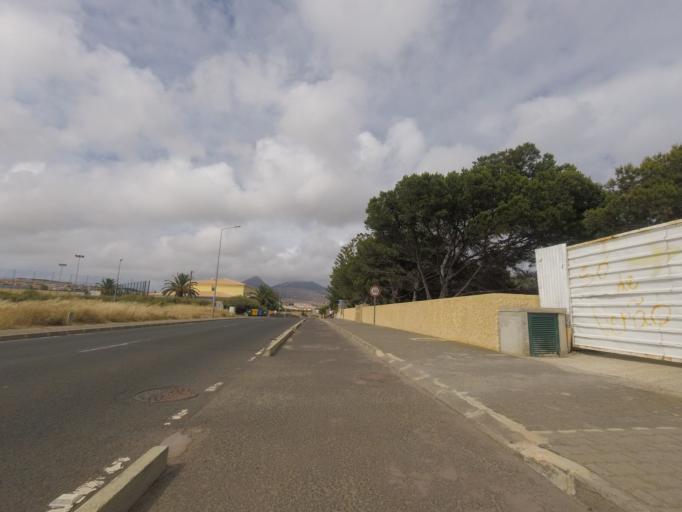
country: PT
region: Madeira
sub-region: Porto Santo
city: Vila de Porto Santo
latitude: 33.0459
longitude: -16.3558
